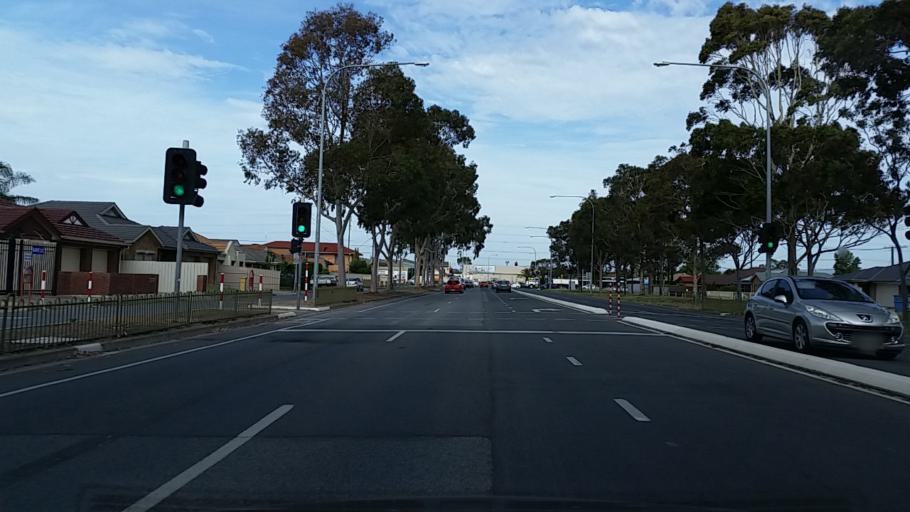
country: AU
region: South Australia
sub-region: Charles Sturt
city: Royal Park
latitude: -34.8795
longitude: 138.5106
